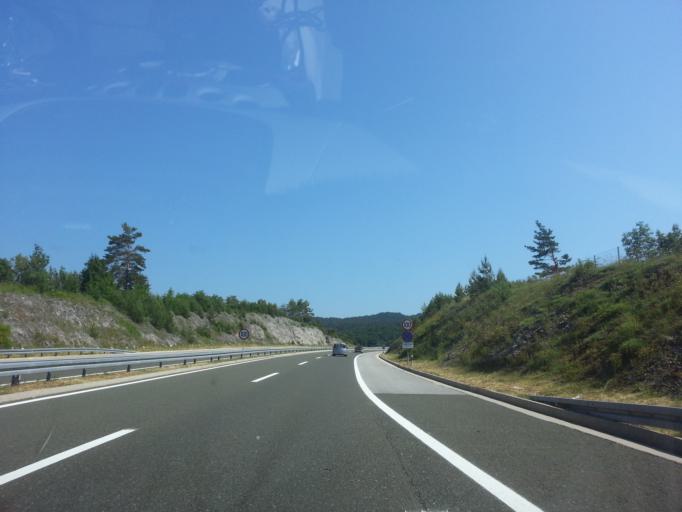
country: HR
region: Primorsko-Goranska
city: Klana
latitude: 45.4790
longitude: 14.2786
